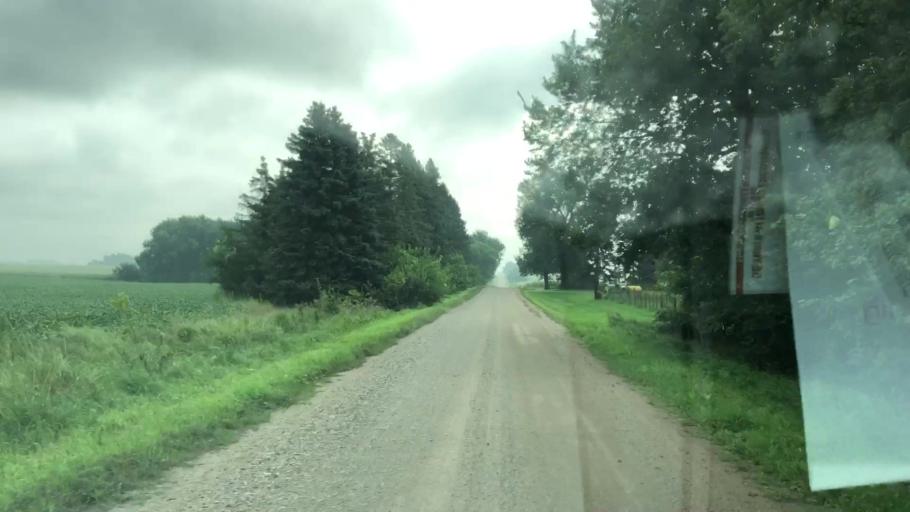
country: US
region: Iowa
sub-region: Lyon County
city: George
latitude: 43.2297
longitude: -96.0136
